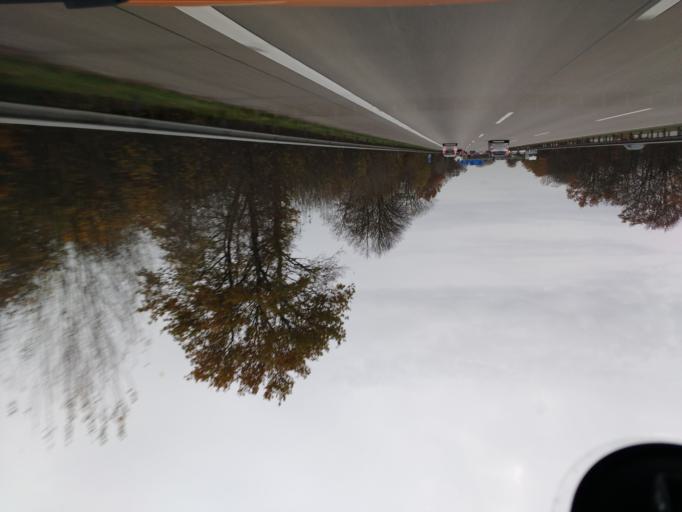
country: DE
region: Bremen
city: Bremen
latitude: 53.0238
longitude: 8.8110
